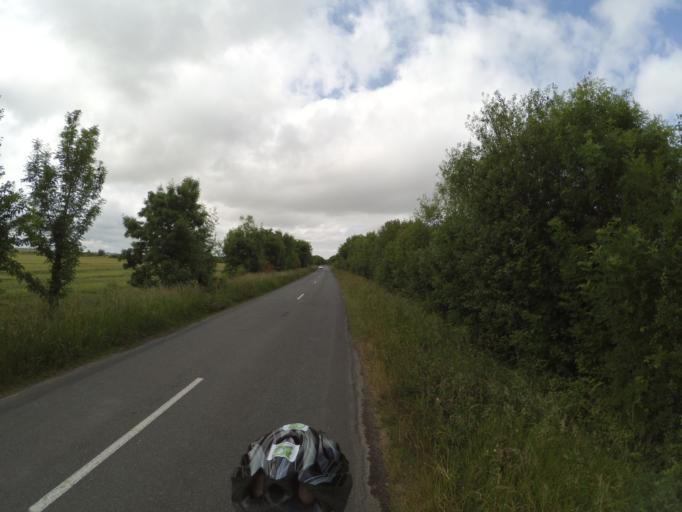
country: FR
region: Poitou-Charentes
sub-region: Departement de la Charente-Maritime
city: Yves
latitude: 46.0411
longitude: -1.0411
